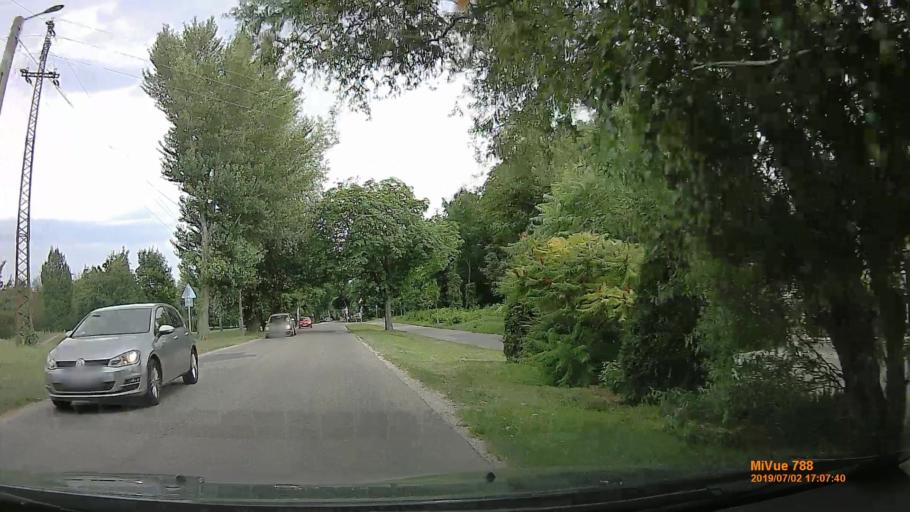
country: HU
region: Gyor-Moson-Sopron
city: Mosonmagyarovar
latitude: 47.8727
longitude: 17.2874
